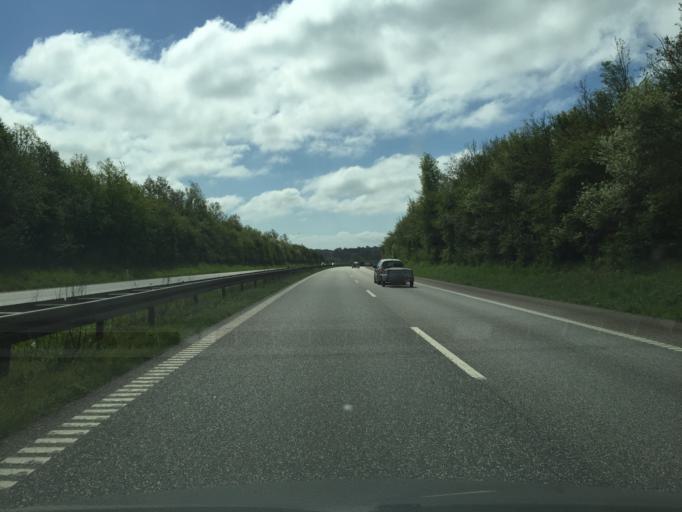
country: DK
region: Zealand
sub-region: Vordingborg Kommune
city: Orslev
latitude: 55.0411
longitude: 11.9883
